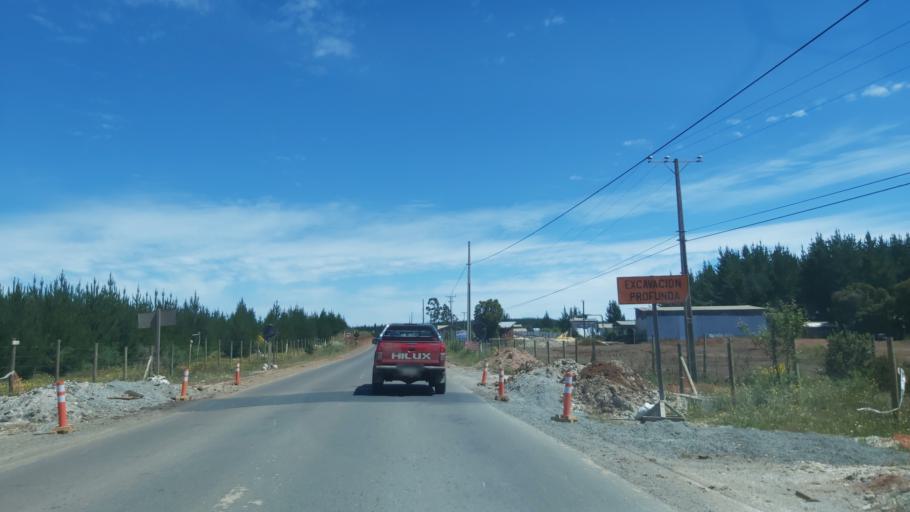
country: CL
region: Maule
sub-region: Provincia de Talca
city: Constitucion
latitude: -35.4008
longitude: -72.4364
